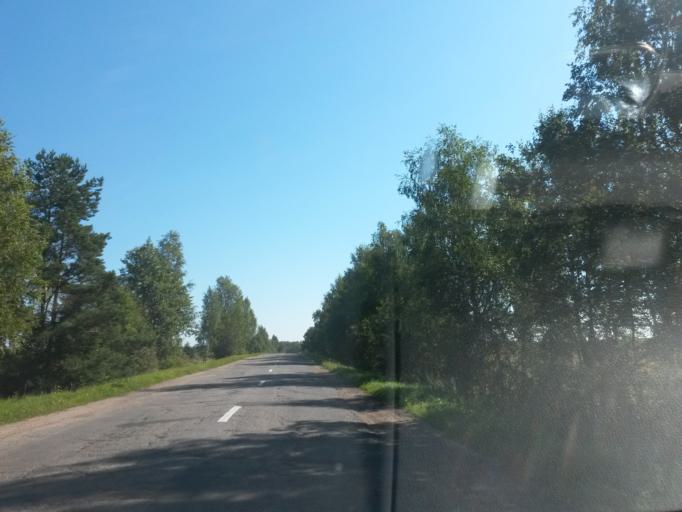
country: RU
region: Jaroslavl
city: Gavrilov-Yam
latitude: 57.3027
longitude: 40.0186
